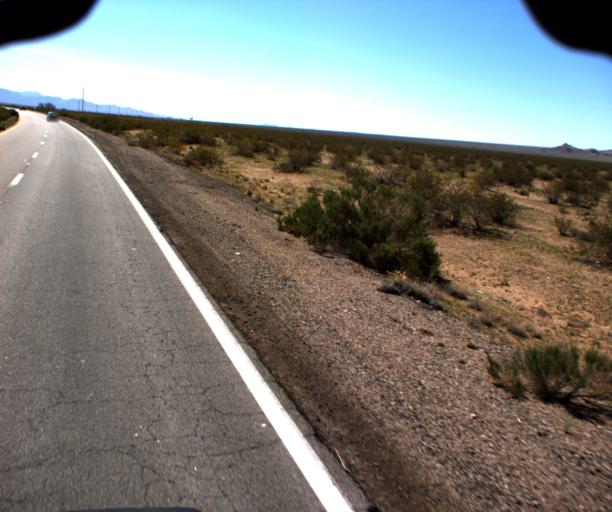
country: US
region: Arizona
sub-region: Mohave County
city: Dolan Springs
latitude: 35.6659
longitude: -114.4560
